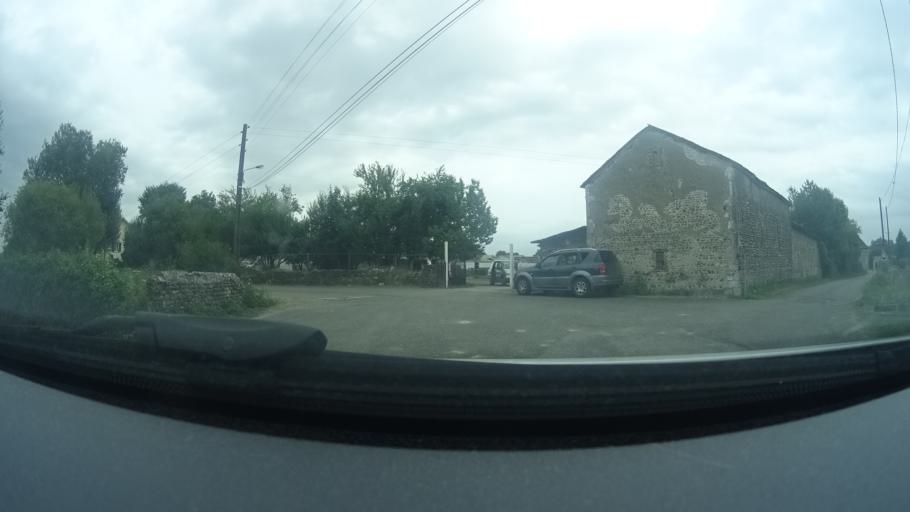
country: FR
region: Aquitaine
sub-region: Departement des Pyrenees-Atlantiques
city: Mont
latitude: 43.4528
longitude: -0.7112
